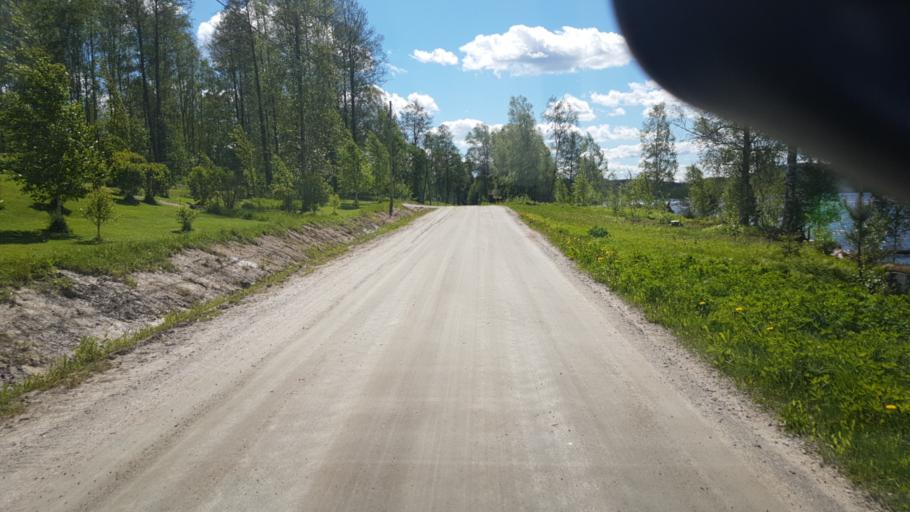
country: SE
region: Vaermland
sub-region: Arvika Kommun
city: Arvika
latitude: 59.7433
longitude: 12.8306
